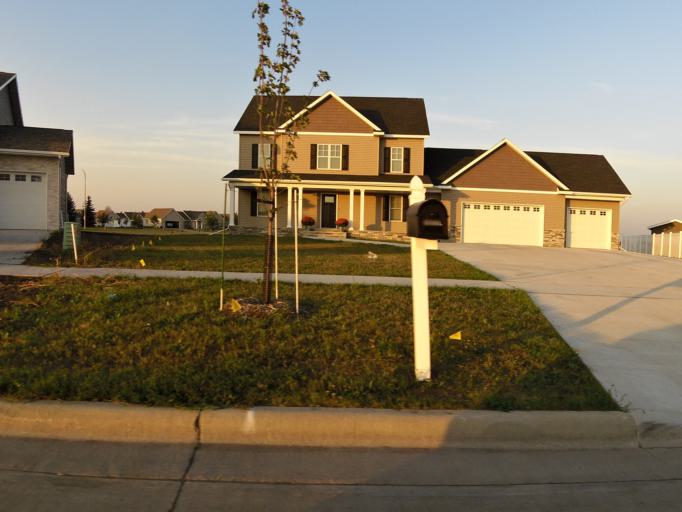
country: US
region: North Dakota
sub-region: Grand Forks County
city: Grand Forks
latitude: 47.8812
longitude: -97.0716
